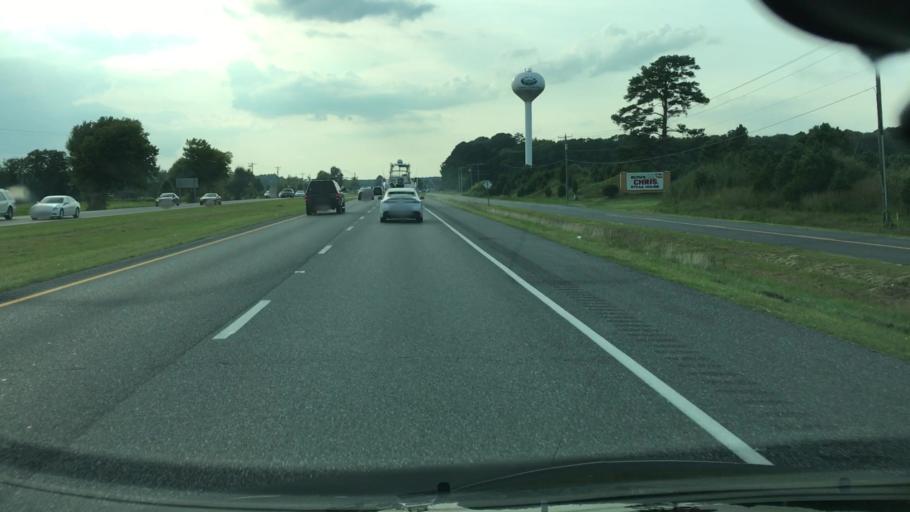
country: US
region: Maryland
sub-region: Worcester County
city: West Ocean City
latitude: 38.3419
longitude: -75.1574
